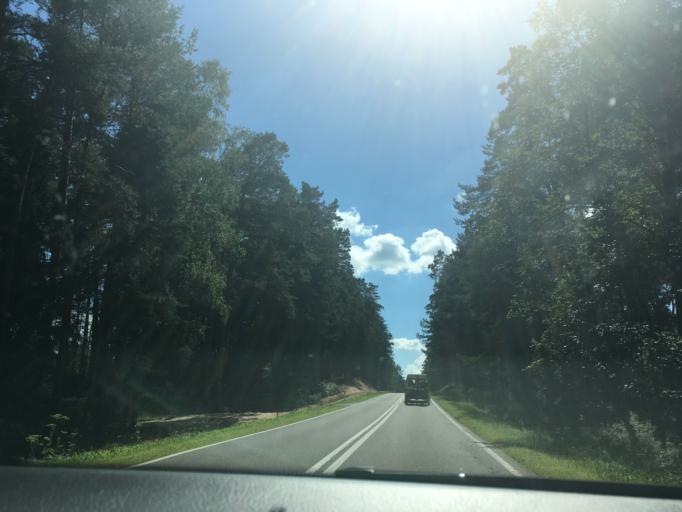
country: PL
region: Podlasie
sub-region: Powiat augustowski
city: Augustow
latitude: 53.8523
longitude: 23.0518
